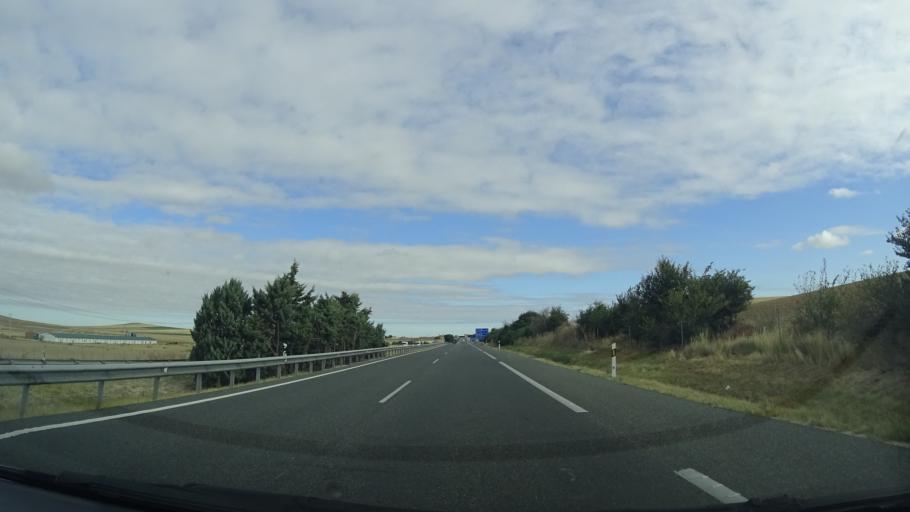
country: ES
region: Castille and Leon
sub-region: Provincia de Valladolid
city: Ataquines
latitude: 41.1655
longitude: -4.7994
